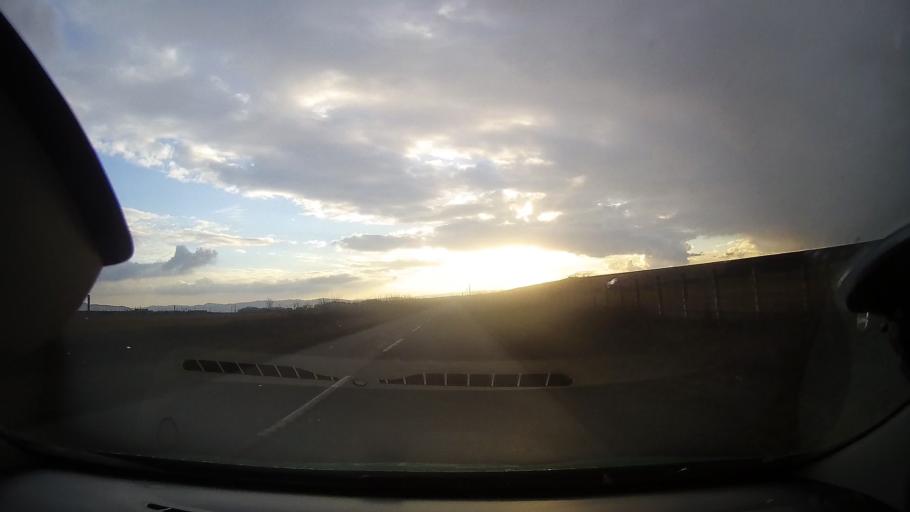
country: RO
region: Alba
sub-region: Comuna Lunca Muresului
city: Lunca Muresului
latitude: 46.4445
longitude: 23.9139
